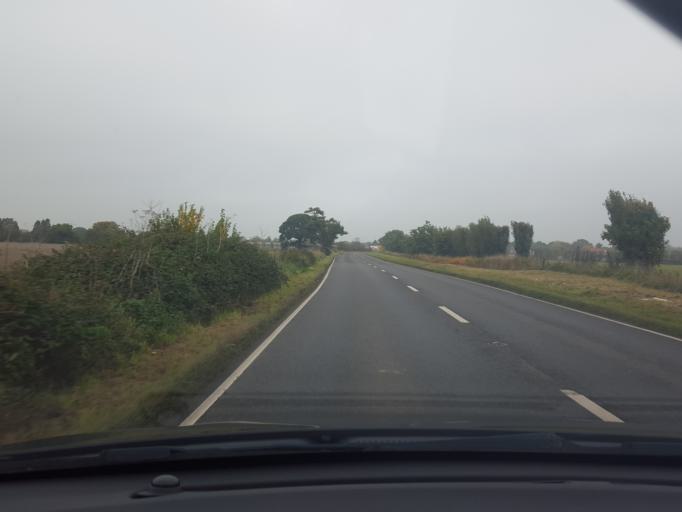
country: GB
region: England
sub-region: Suffolk
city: East Bergholt
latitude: 51.9275
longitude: 0.9927
